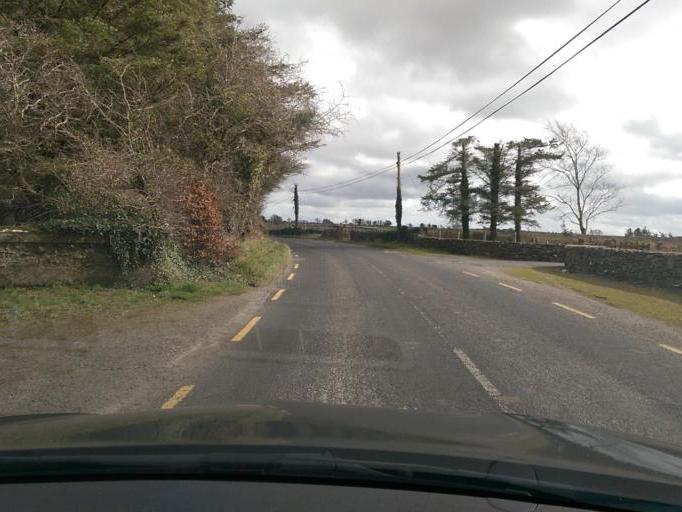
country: IE
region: Connaught
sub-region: County Galway
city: Loughrea
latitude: 53.4194
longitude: -8.5234
